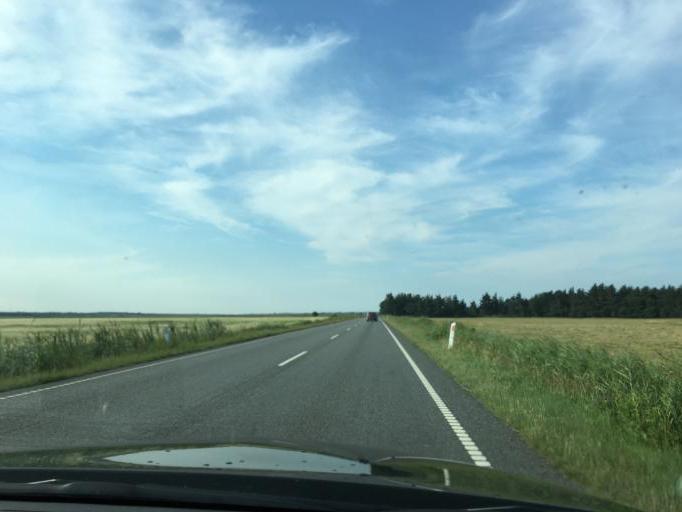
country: DK
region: Central Jutland
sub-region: Ringkobing-Skjern Kommune
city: Hvide Sande
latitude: 55.8559
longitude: 8.1784
